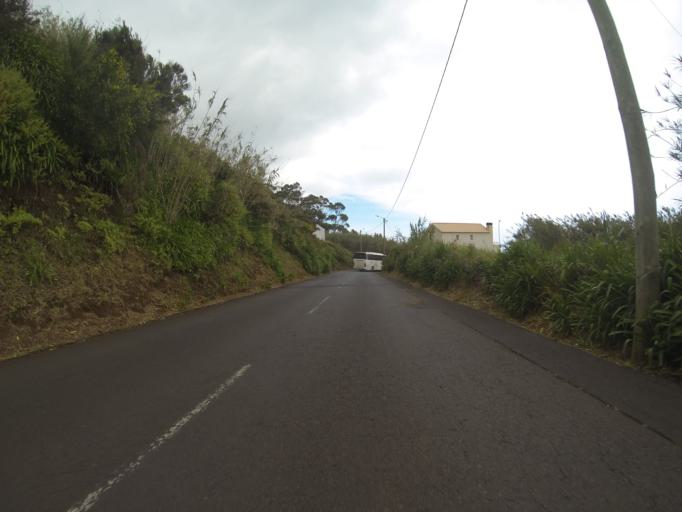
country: PT
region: Madeira
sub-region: Porto Moniz
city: Porto Moniz
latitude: 32.8609
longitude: -17.1730
